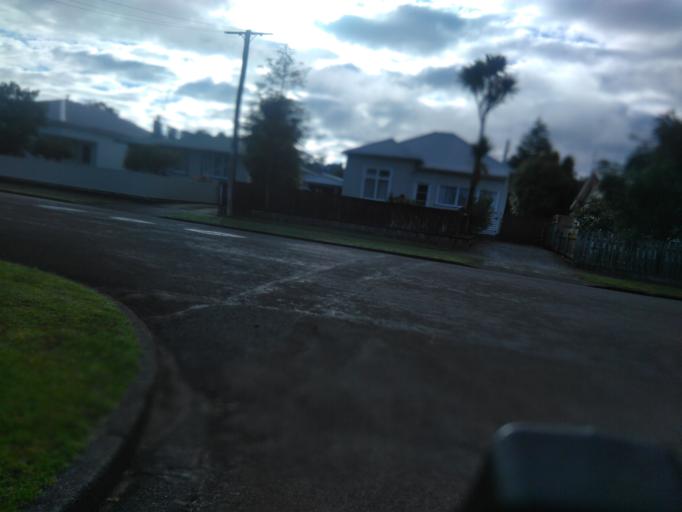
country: NZ
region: Gisborne
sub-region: Gisborne District
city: Gisborne
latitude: -38.6460
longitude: 178.0166
